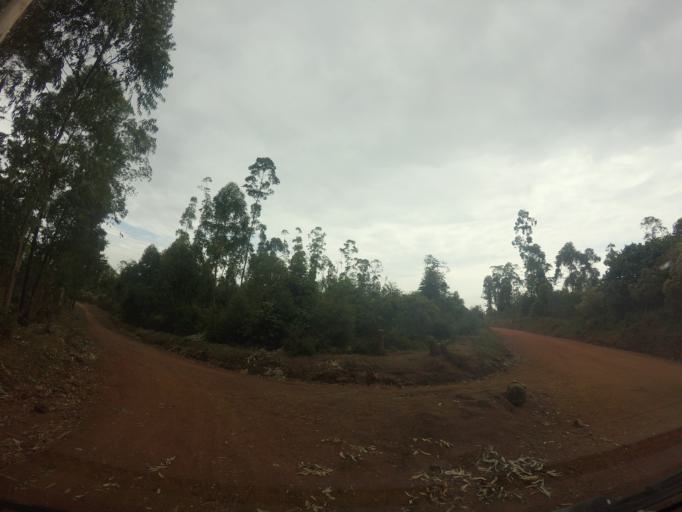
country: UG
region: Northern Region
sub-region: Arua District
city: Arua
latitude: 2.7686
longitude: 30.8589
